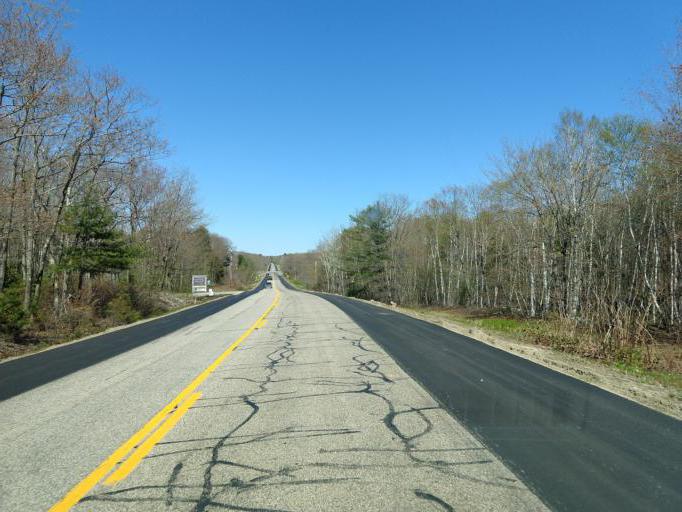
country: US
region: Maine
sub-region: York County
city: Arundel
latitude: 43.4022
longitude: -70.4318
